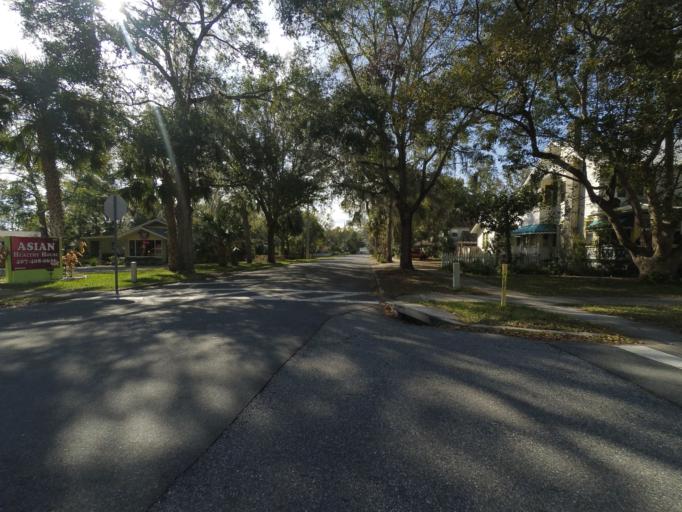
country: US
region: Florida
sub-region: Lake County
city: Mount Dora
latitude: 28.8033
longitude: -81.6447
